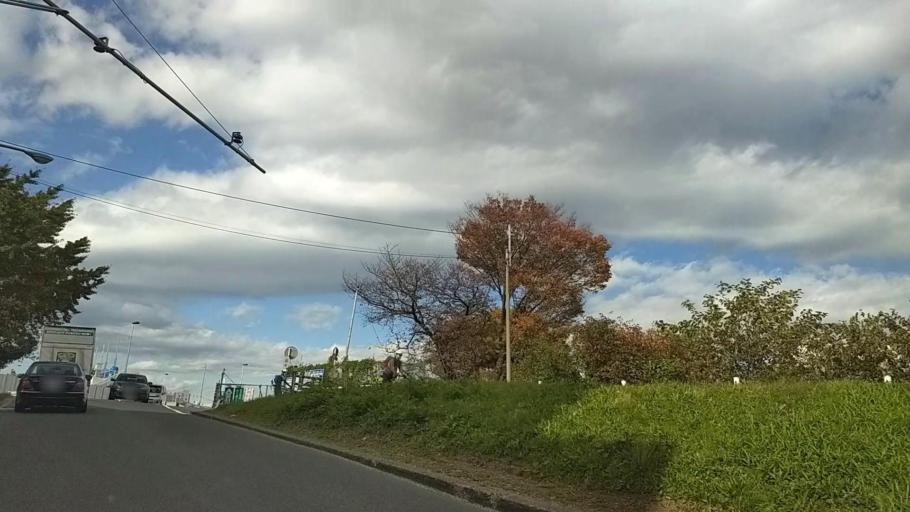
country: JP
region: Tokyo
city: Chofugaoka
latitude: 35.6225
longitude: 139.5693
